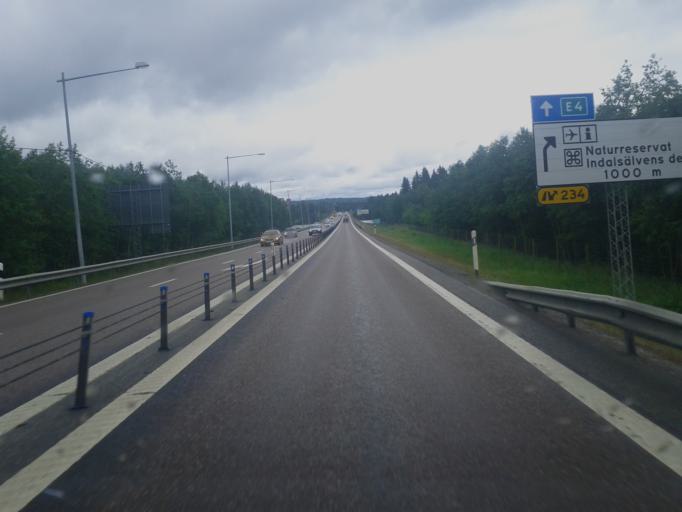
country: SE
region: Vaesternorrland
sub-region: Timra Kommun
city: Bergeforsen
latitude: 62.5175
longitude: 17.4167
